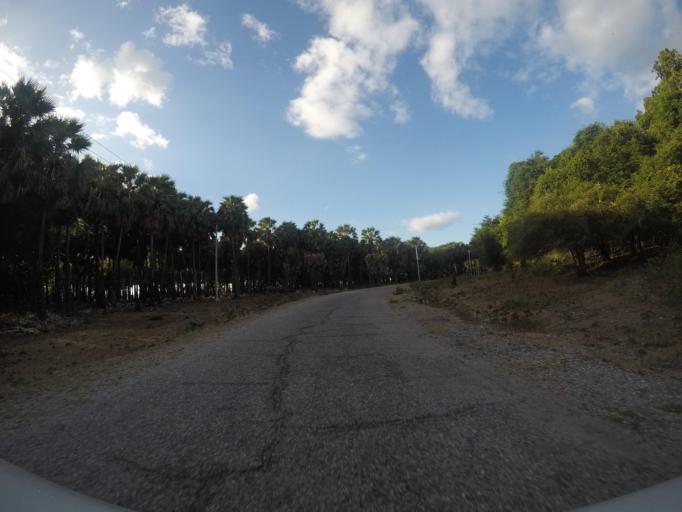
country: TL
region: Lautem
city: Lospalos
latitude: -8.3311
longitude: 126.9570
